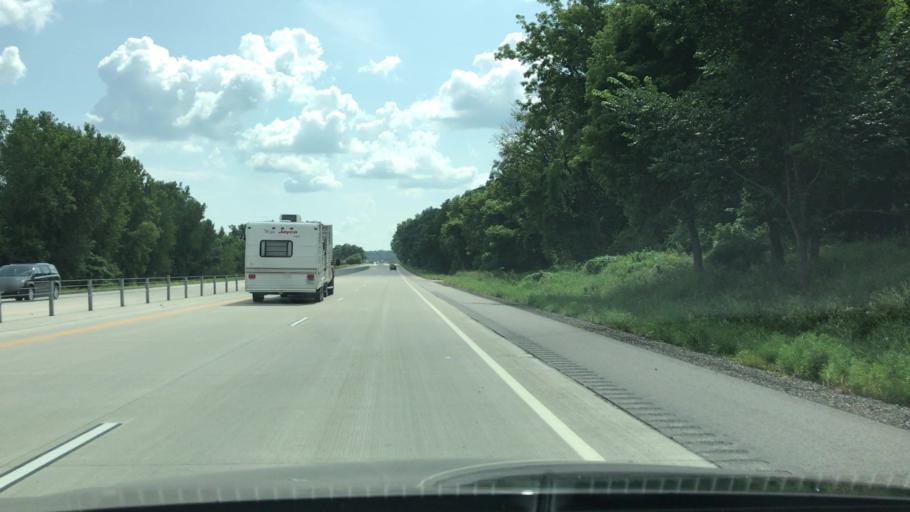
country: US
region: Minnesota
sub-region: Nicollet County
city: Saint Peter
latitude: 44.2818
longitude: -94.0086
